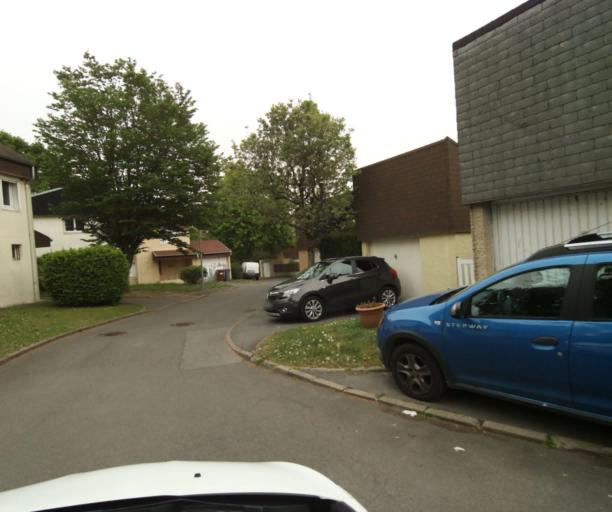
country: FR
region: Ile-de-France
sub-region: Departement de Seine-et-Marne
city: Noisiel
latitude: 48.8491
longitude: 2.6362
